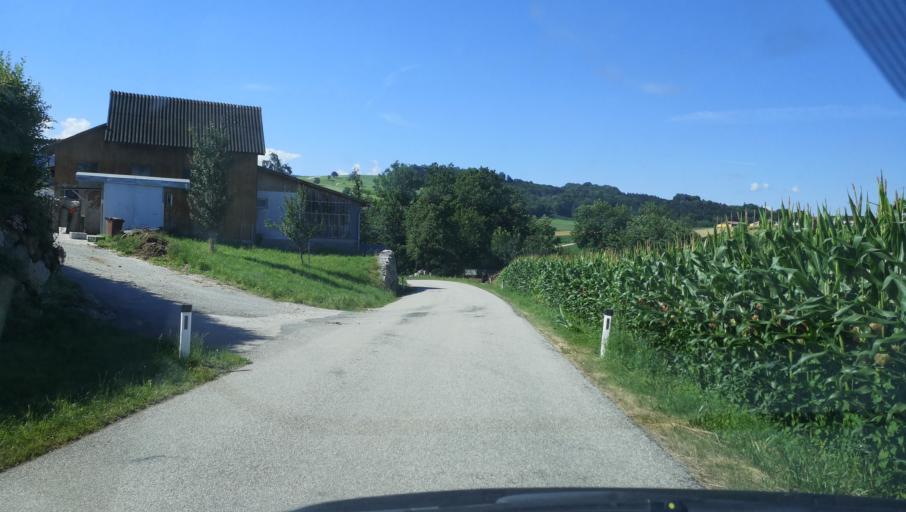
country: AT
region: Lower Austria
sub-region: Politischer Bezirk Amstetten
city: Euratsfeld
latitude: 48.0661
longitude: 14.9232
